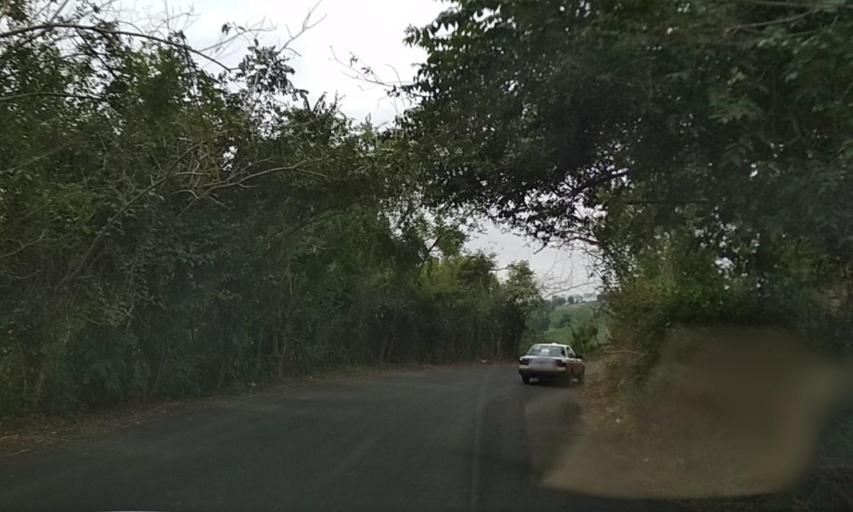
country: MX
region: Veracruz
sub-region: Coatzintla
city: Manuel Maria Contreras
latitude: 20.4457
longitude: -97.4997
